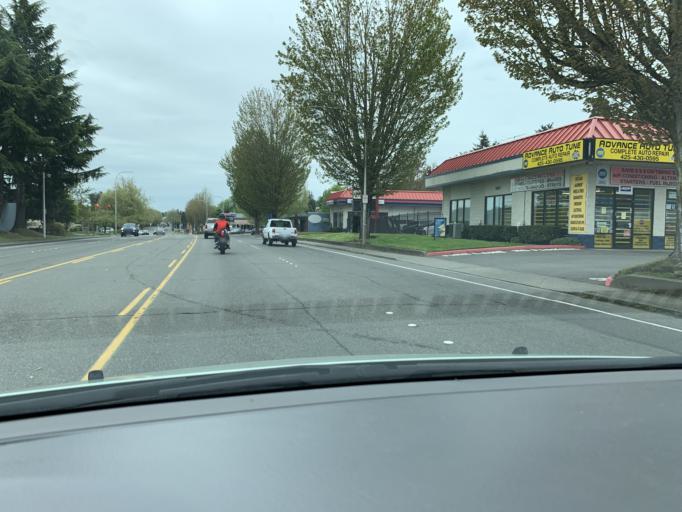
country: US
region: Washington
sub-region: King County
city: Renton
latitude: 47.4882
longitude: -122.2180
